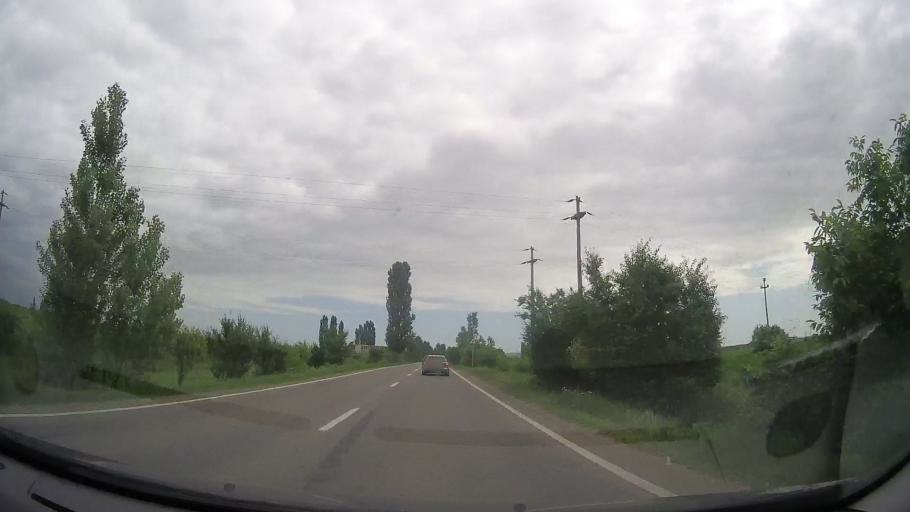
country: RO
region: Prahova
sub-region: Comuna Barcanesti
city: Barcanesti
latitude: 44.8917
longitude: 26.0495
